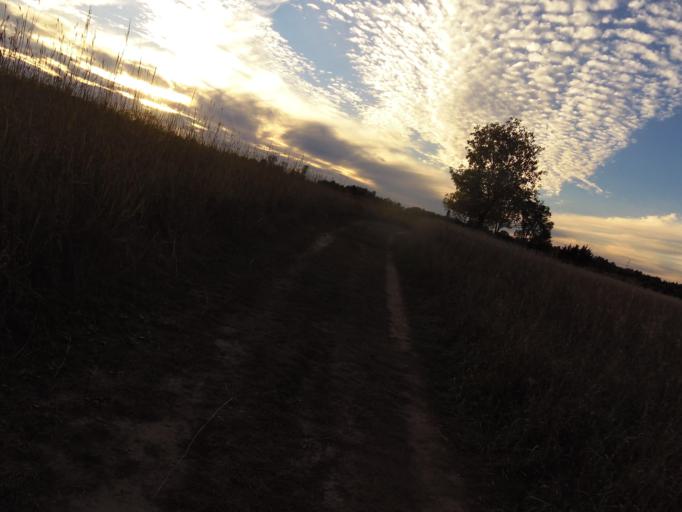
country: US
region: Minnesota
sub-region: Washington County
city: Afton
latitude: 44.8721
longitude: -92.7907
